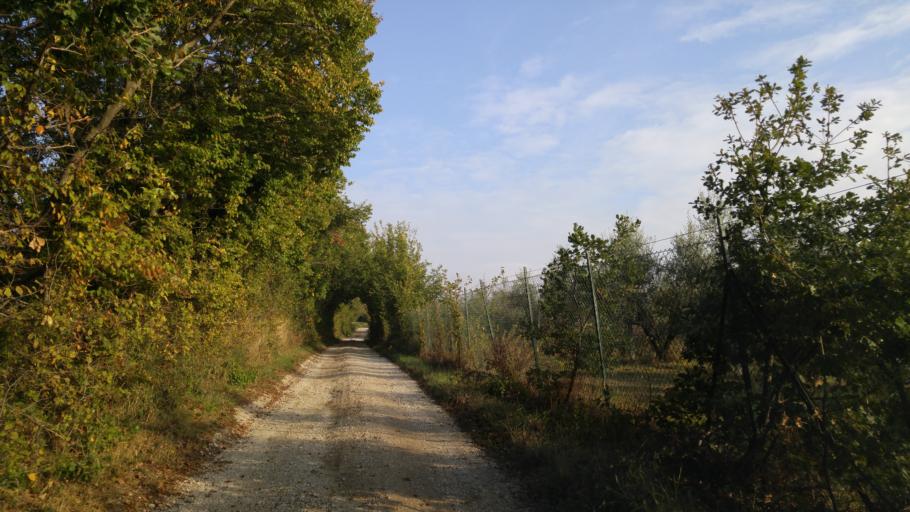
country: IT
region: The Marches
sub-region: Provincia di Pesaro e Urbino
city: Fenile
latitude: 43.8719
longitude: 12.9654
